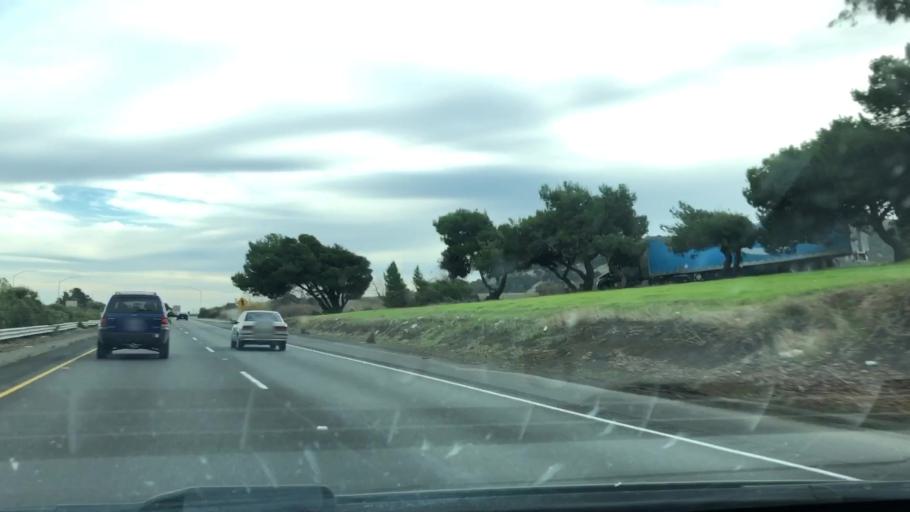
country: US
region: California
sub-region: Solano County
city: Benicia
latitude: 38.1483
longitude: -122.1112
